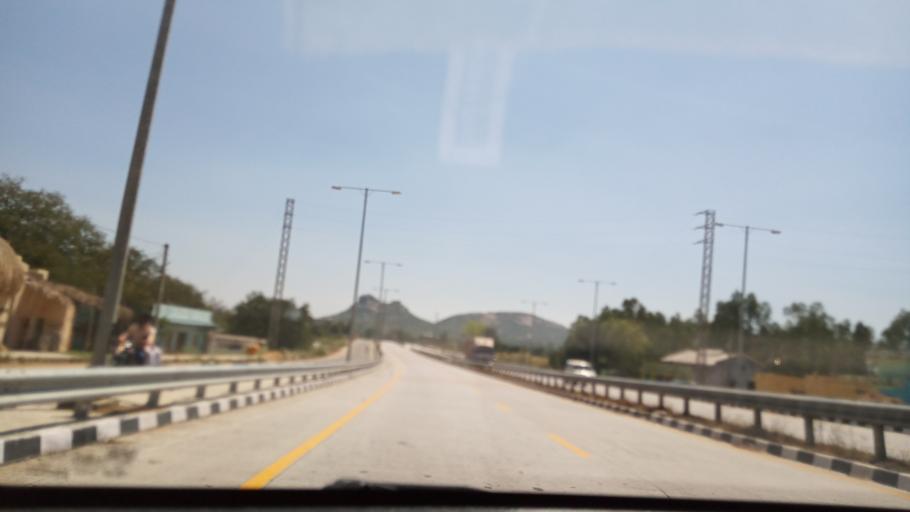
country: IN
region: Andhra Pradesh
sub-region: Chittoor
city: Palmaner
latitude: 13.1814
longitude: 78.6199
